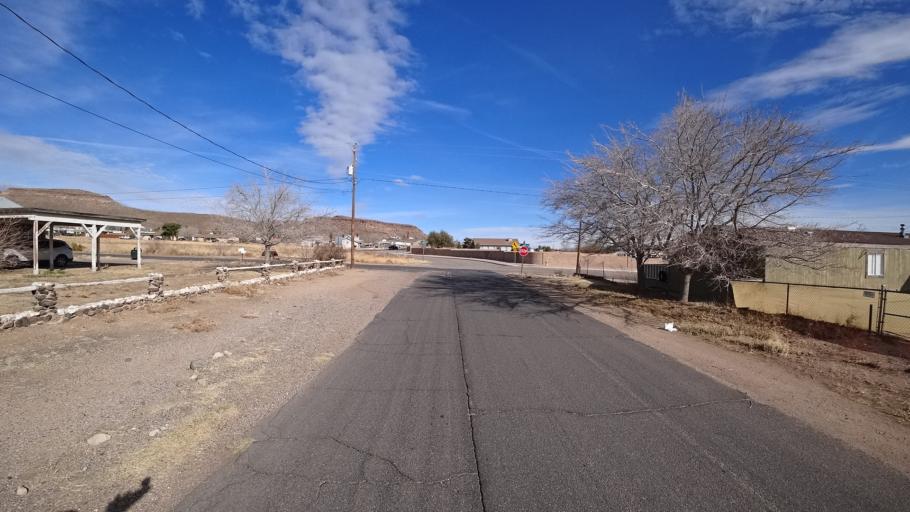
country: US
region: Arizona
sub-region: Mohave County
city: Kingman
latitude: 35.2182
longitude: -114.0490
